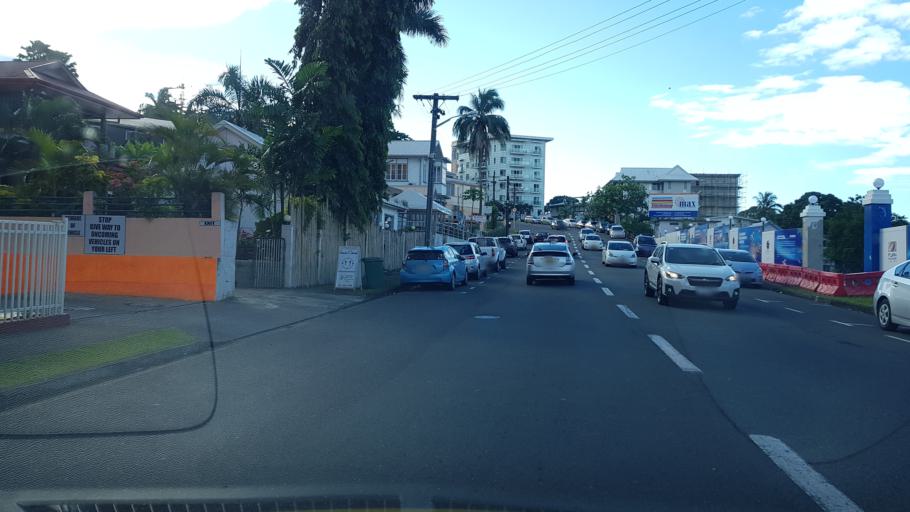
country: FJ
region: Central
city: Suva
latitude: -18.1443
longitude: 178.4263
